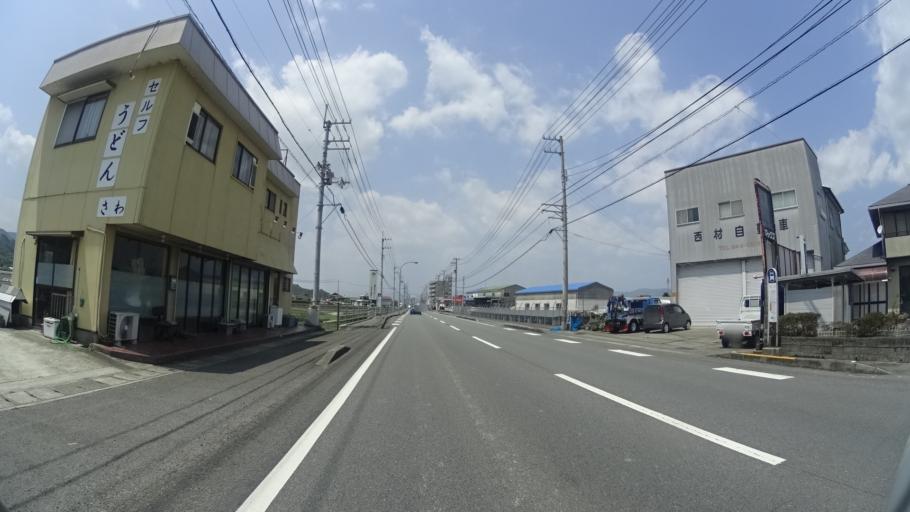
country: JP
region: Tokushima
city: Ishii
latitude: 34.0695
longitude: 134.4077
